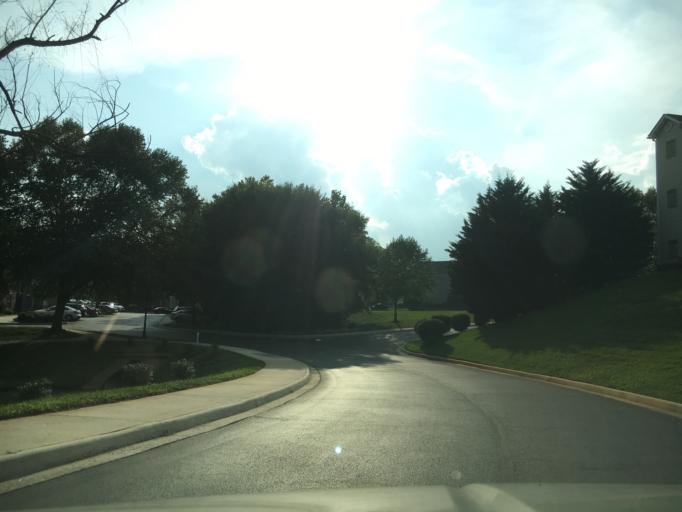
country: US
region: Virginia
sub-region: Campbell County
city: Timberlake
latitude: 37.3376
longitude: -79.2333
